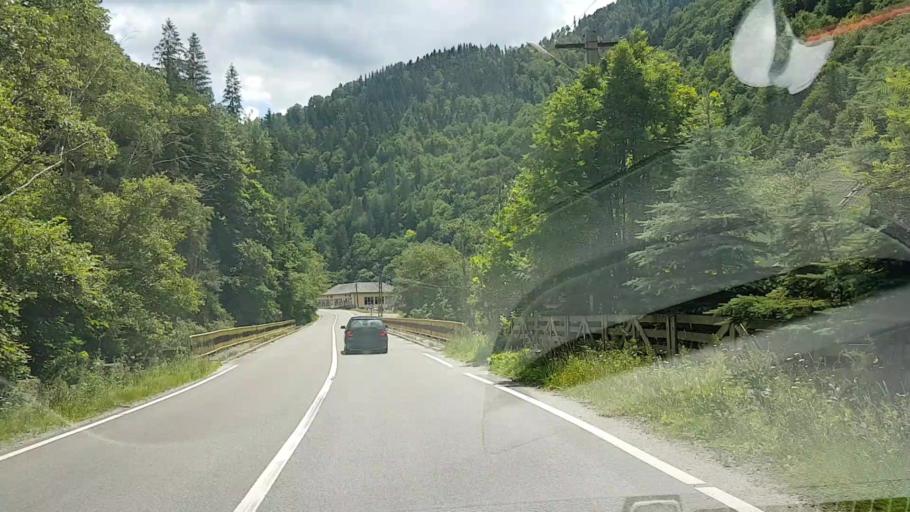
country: RO
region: Suceava
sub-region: Comuna Crucea
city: Crucea
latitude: 47.2856
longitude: 25.6358
